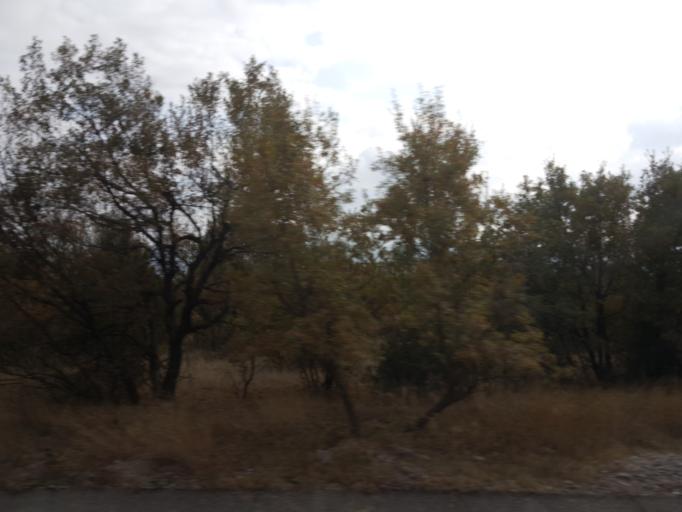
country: TR
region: Sinop
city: Sarayduzu
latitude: 41.3392
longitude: 34.7921
